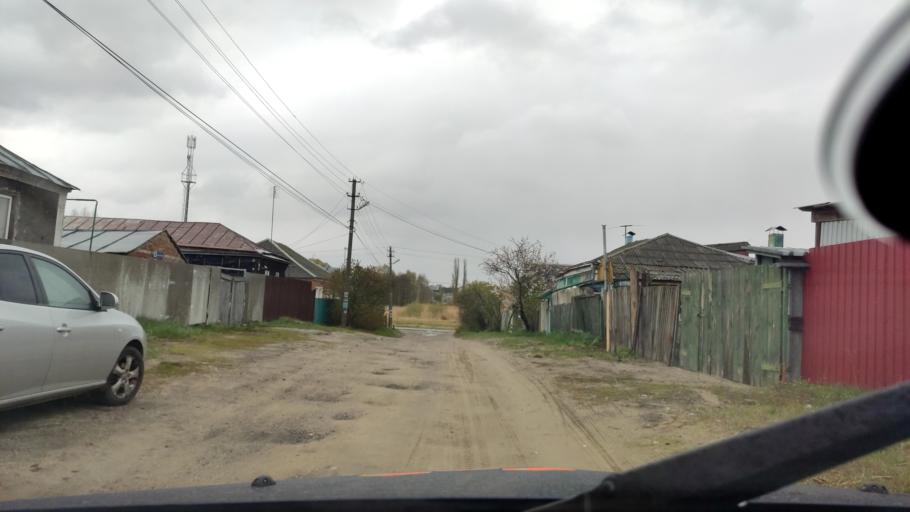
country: RU
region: Voronezj
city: Voronezh
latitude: 51.7403
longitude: 39.2625
